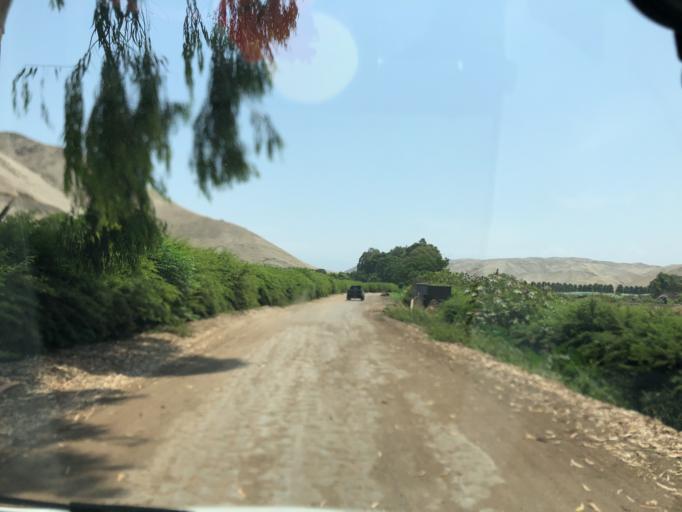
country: PE
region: Lima
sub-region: Provincia de Canete
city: San Vicente de Canete
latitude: -13.0102
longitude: -76.4618
